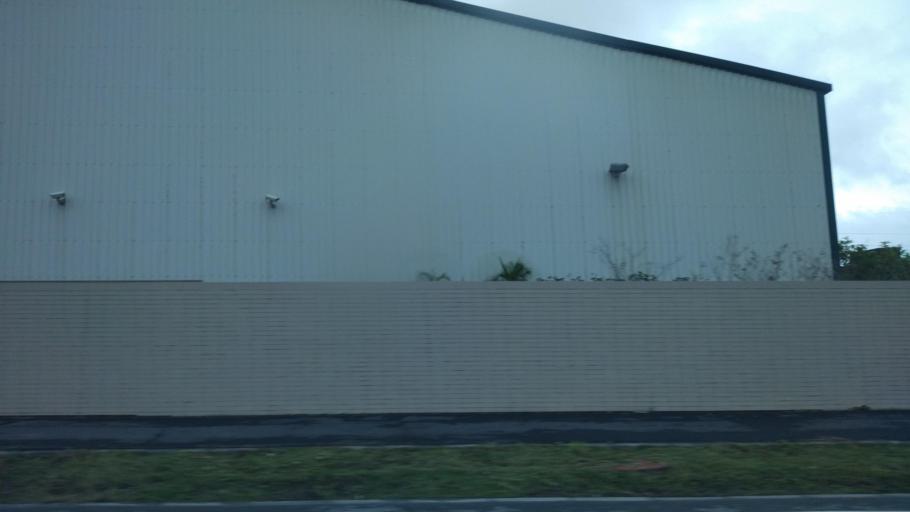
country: TW
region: Taiwan
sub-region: Yilan
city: Yilan
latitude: 24.6118
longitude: 121.8345
